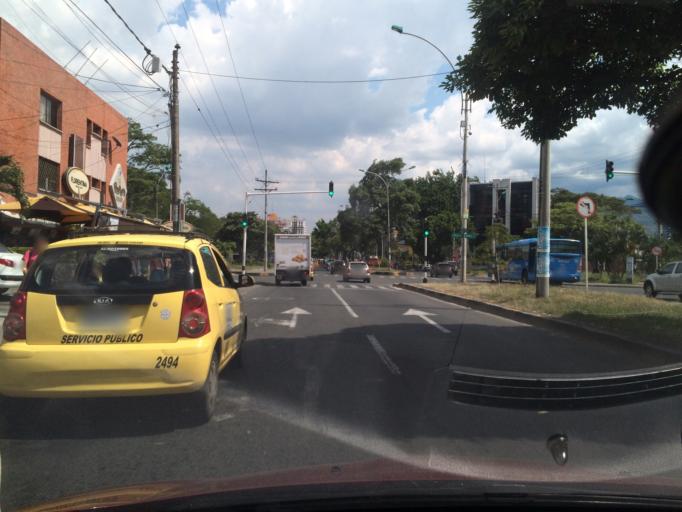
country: CO
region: Valle del Cauca
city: Cali
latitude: 3.4272
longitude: -76.5395
